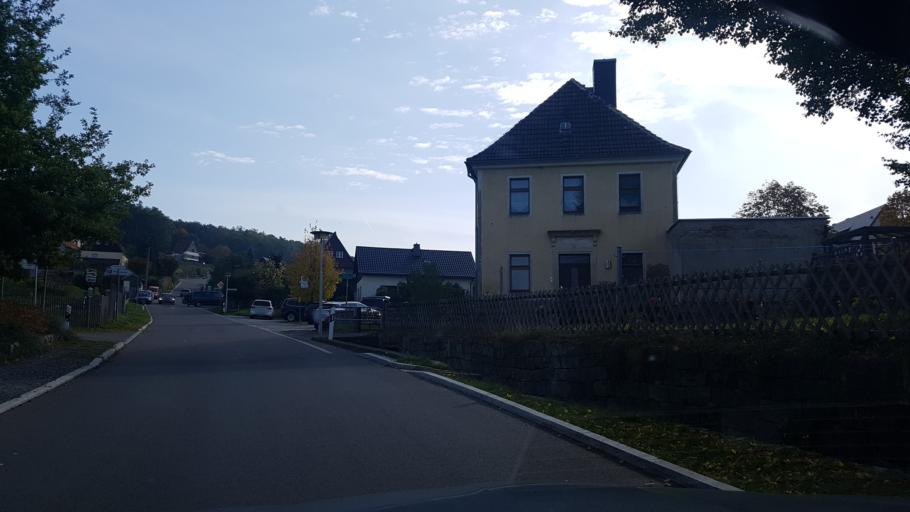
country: DE
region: Saxony
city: Konigstein
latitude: 50.9073
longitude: 14.0802
